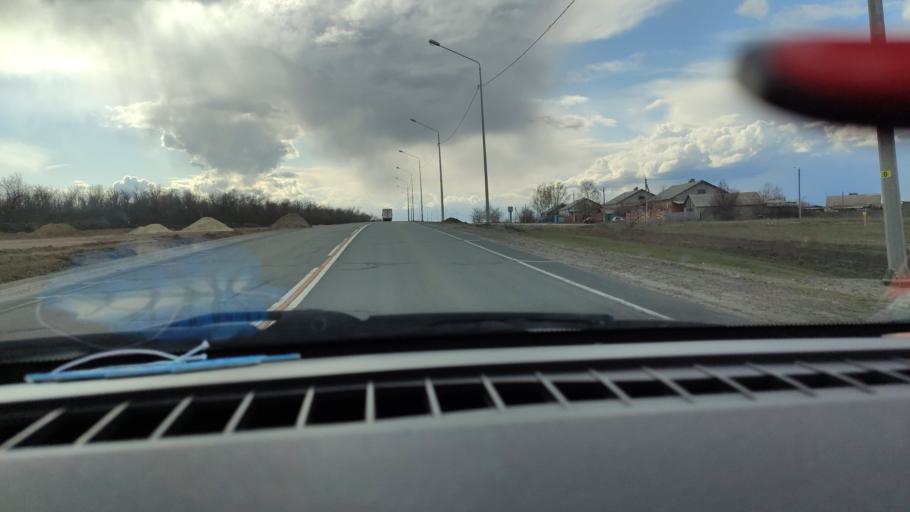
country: RU
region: Saratov
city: Sennoy
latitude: 52.1592
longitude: 47.0605
